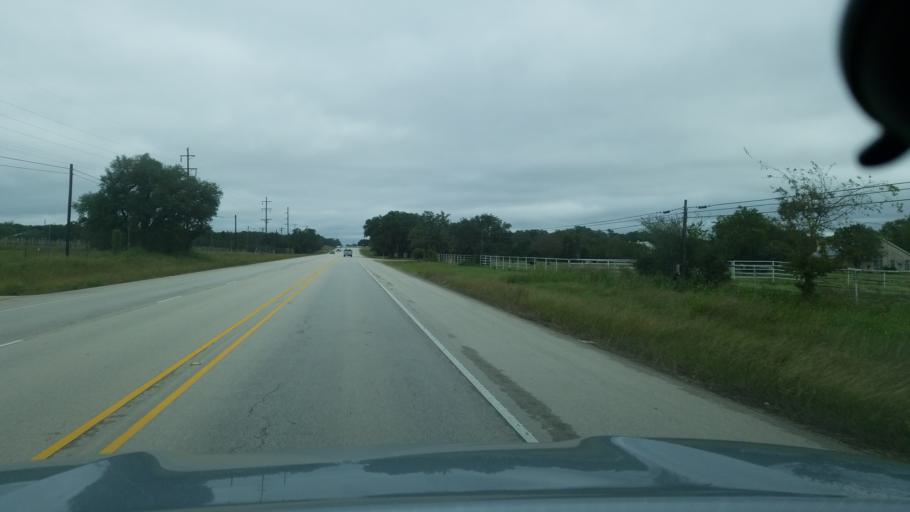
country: US
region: Texas
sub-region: Blanco County
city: Blanco
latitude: 30.0592
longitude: -98.4112
